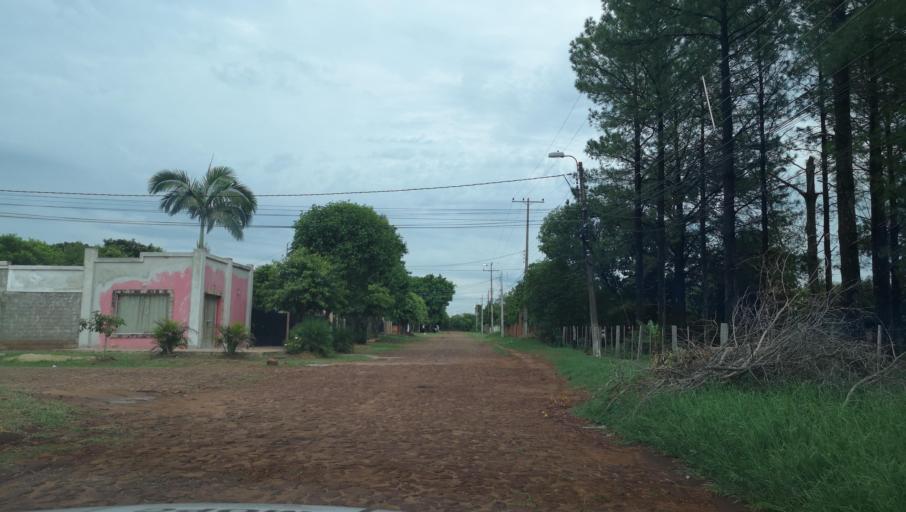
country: PY
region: Misiones
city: Santa Maria
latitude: -26.8873
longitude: -57.0421
